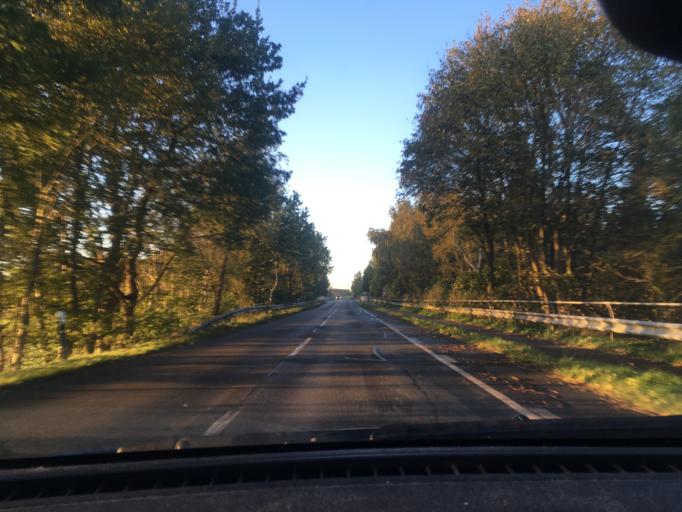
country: DE
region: Lower Saxony
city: Wendisch Evern
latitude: 53.2171
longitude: 10.4645
